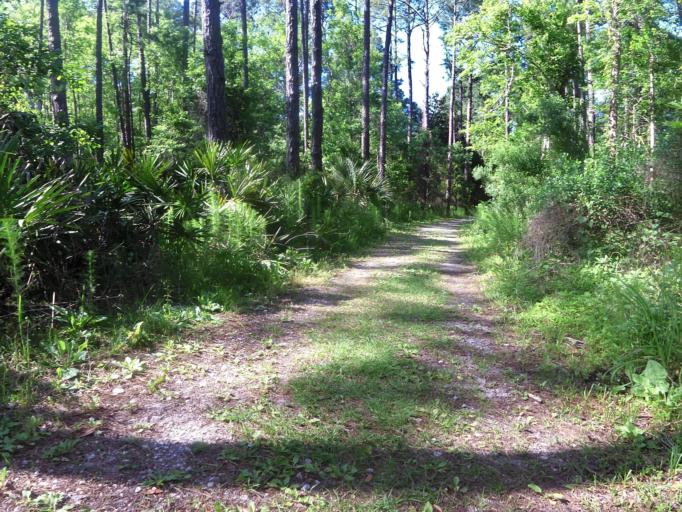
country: US
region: Florida
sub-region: Duval County
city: Atlantic Beach
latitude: 30.4596
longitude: -81.4866
